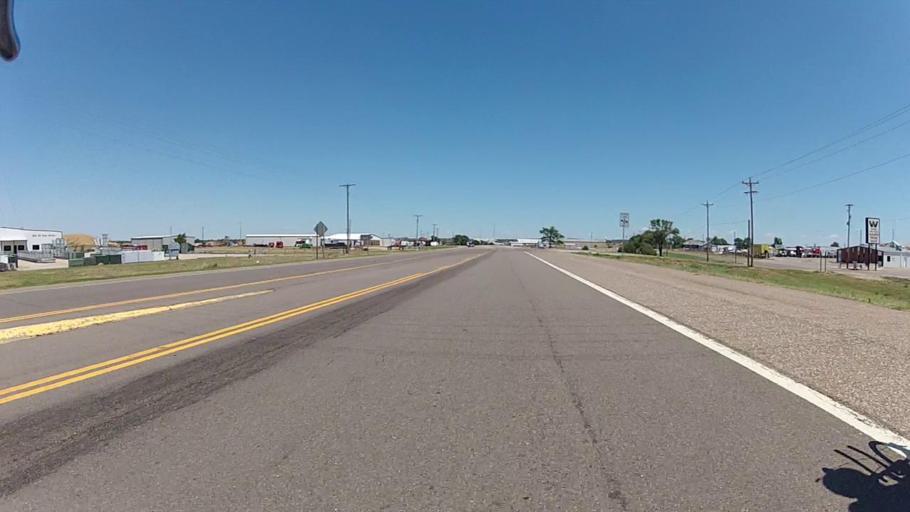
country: US
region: Kansas
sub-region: Ford County
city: Dodge City
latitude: 37.7229
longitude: -100.0154
